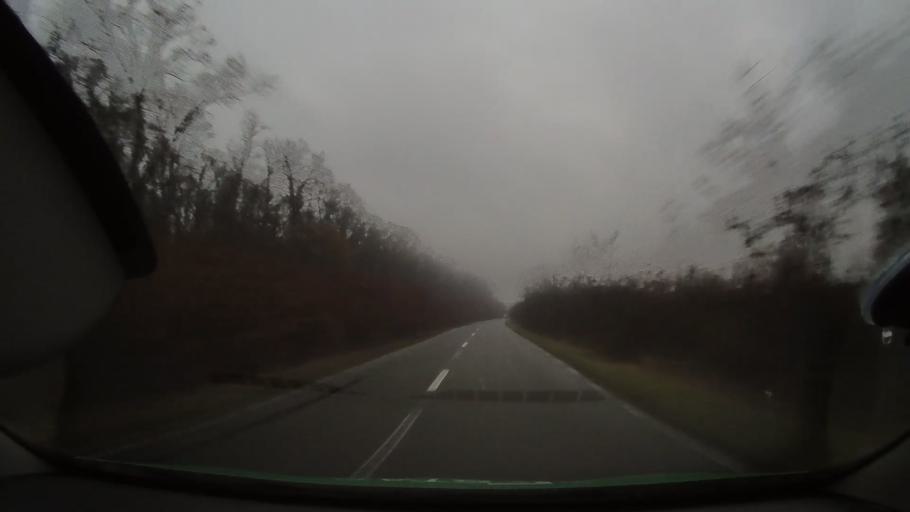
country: RO
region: Arad
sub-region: Comuna Craiova
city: Craiova
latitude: 46.5331
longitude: 21.9556
